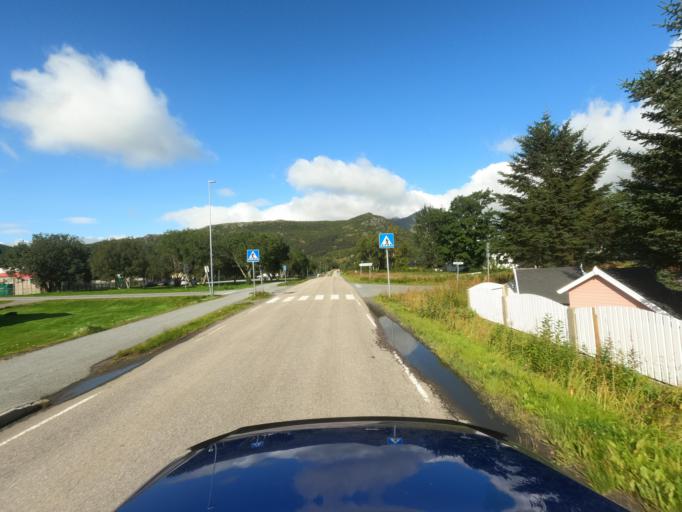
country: NO
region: Nordland
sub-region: Vestvagoy
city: Evjen
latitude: 68.1374
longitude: 13.8379
